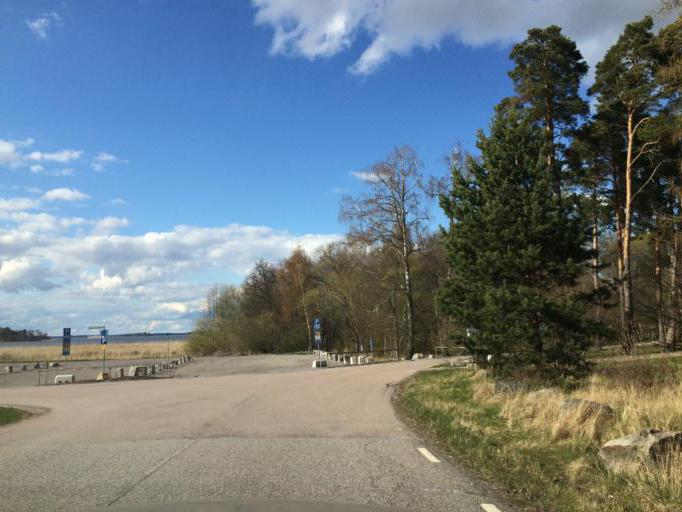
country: SE
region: Soedermanland
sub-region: Eskilstuna Kommun
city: Eskilstuna
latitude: 59.4456
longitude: 16.6214
